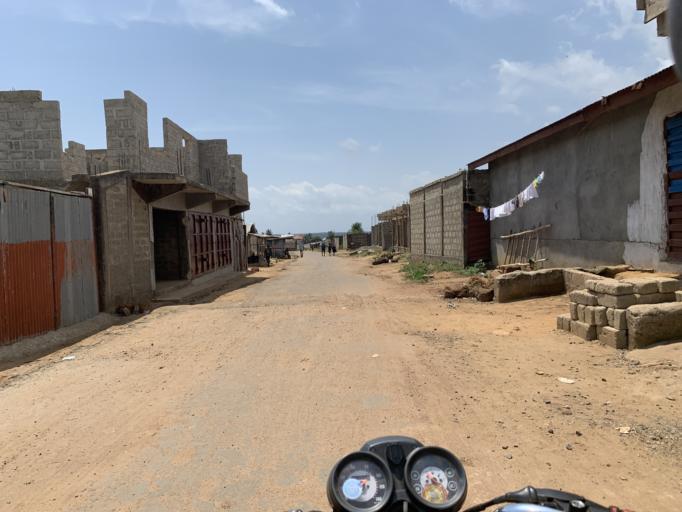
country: SL
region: Western Area
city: Waterloo
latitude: 8.3369
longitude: -13.0324
